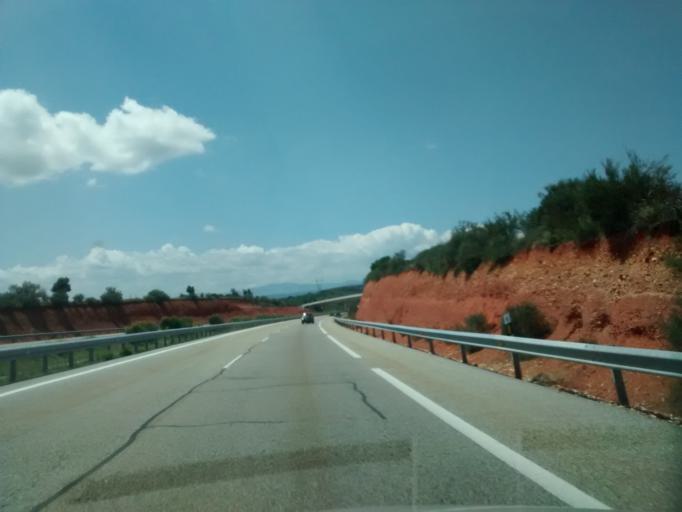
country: ES
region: Castille and Leon
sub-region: Provincia de Leon
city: Brazuelo
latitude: 42.5025
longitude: -6.1199
